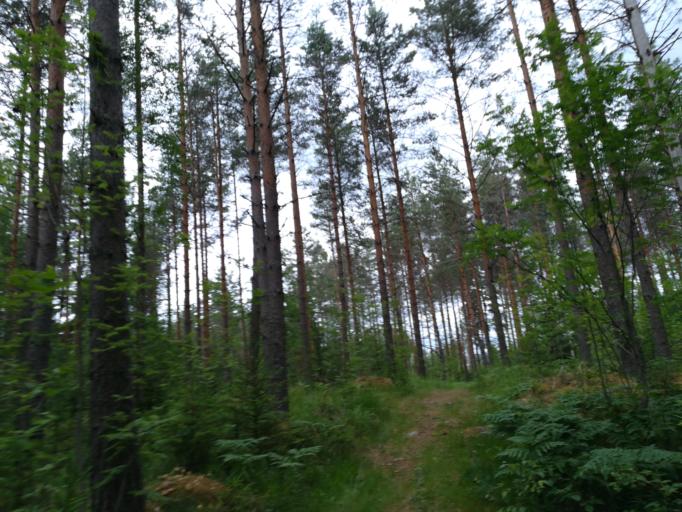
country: FI
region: South Karelia
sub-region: Lappeenranta
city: Savitaipale
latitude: 61.2599
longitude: 27.7085
